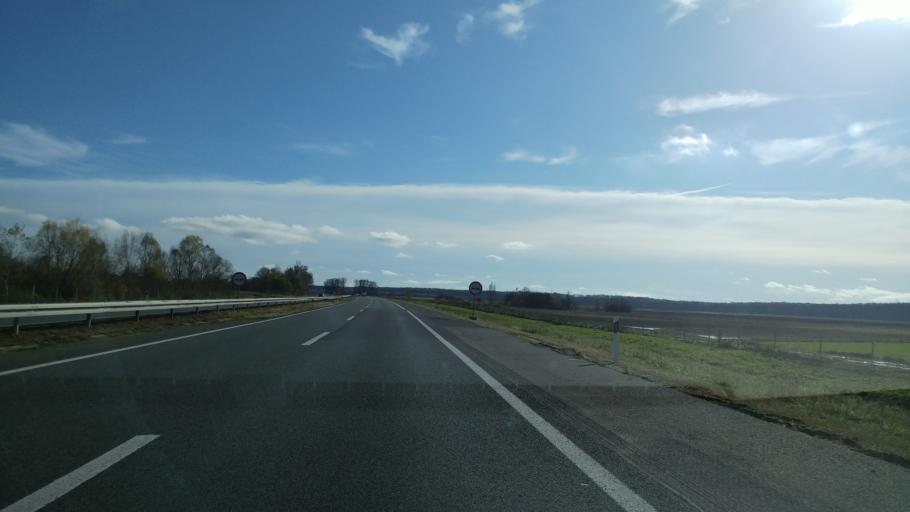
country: HR
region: Sisacko-Moslavacka
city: Lipovljani
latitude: 45.3862
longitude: 16.8693
